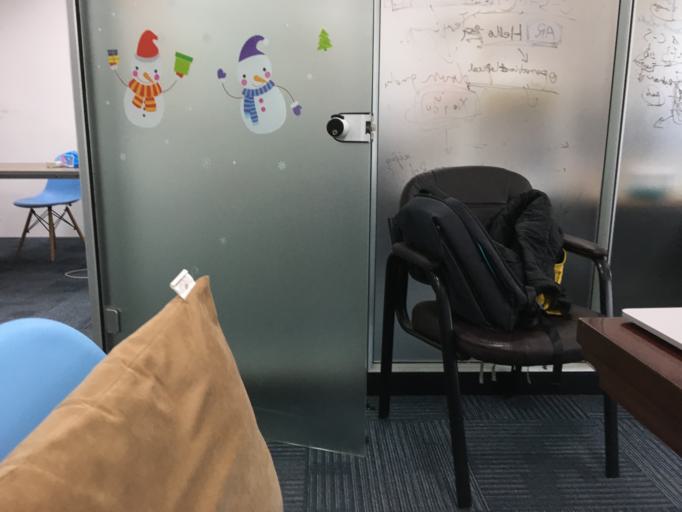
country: CN
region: Guangdong
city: Guicheng
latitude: 23.0346
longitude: 113.1814
